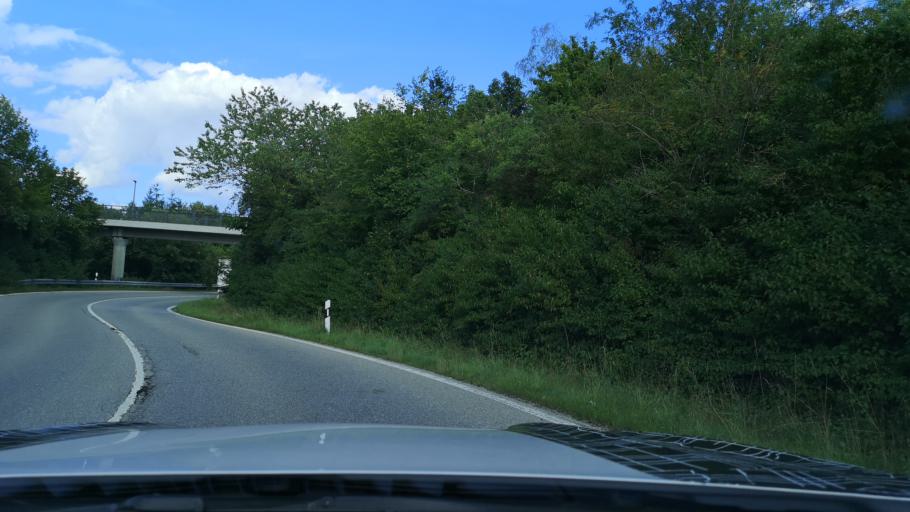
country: DE
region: Bavaria
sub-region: Upper Bavaria
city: Kirchheim bei Muenchen
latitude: 48.1712
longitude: 11.7524
